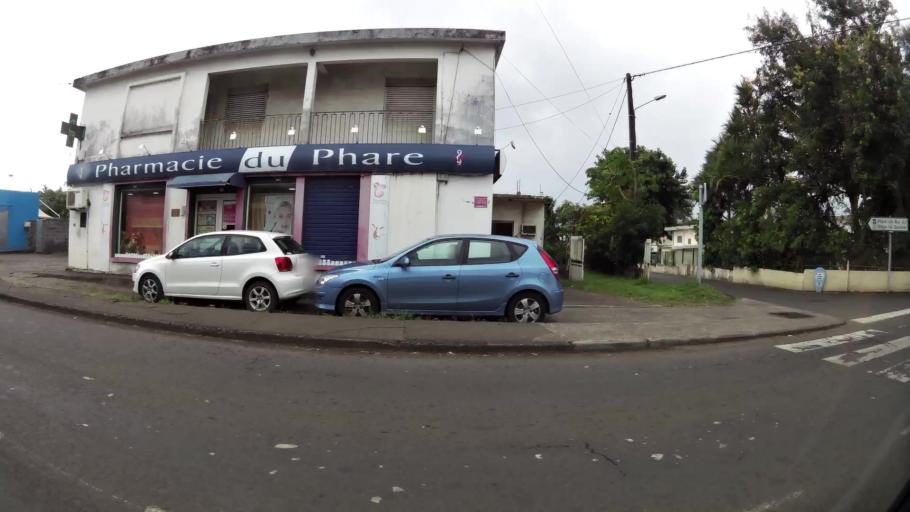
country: RE
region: Reunion
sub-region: Reunion
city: Sainte-Suzanne
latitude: -20.9033
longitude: 55.6009
